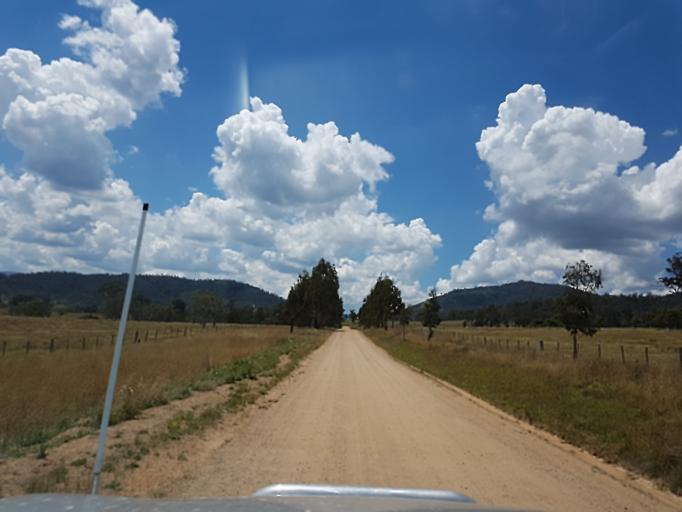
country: AU
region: Victoria
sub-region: Alpine
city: Mount Beauty
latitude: -36.8995
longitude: 147.8695
